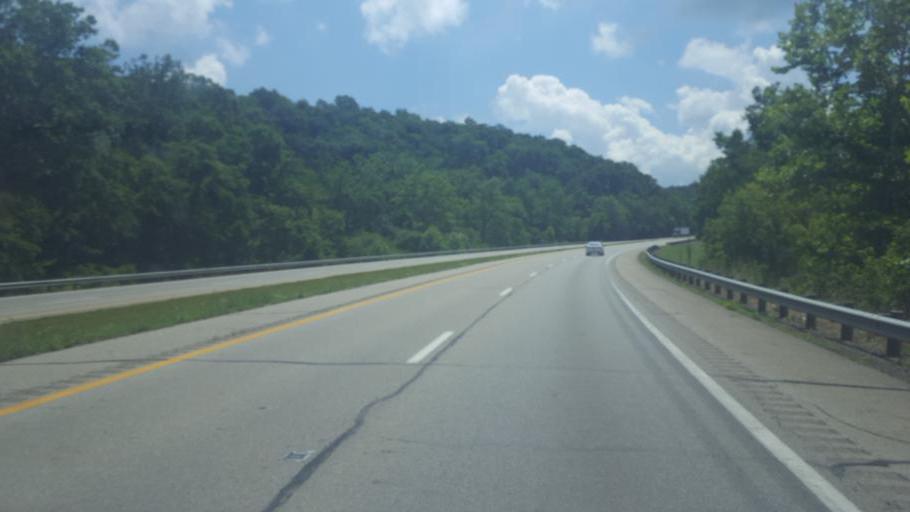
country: US
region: Ohio
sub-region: Jackson County
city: Jackson
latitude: 39.1518
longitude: -82.7296
